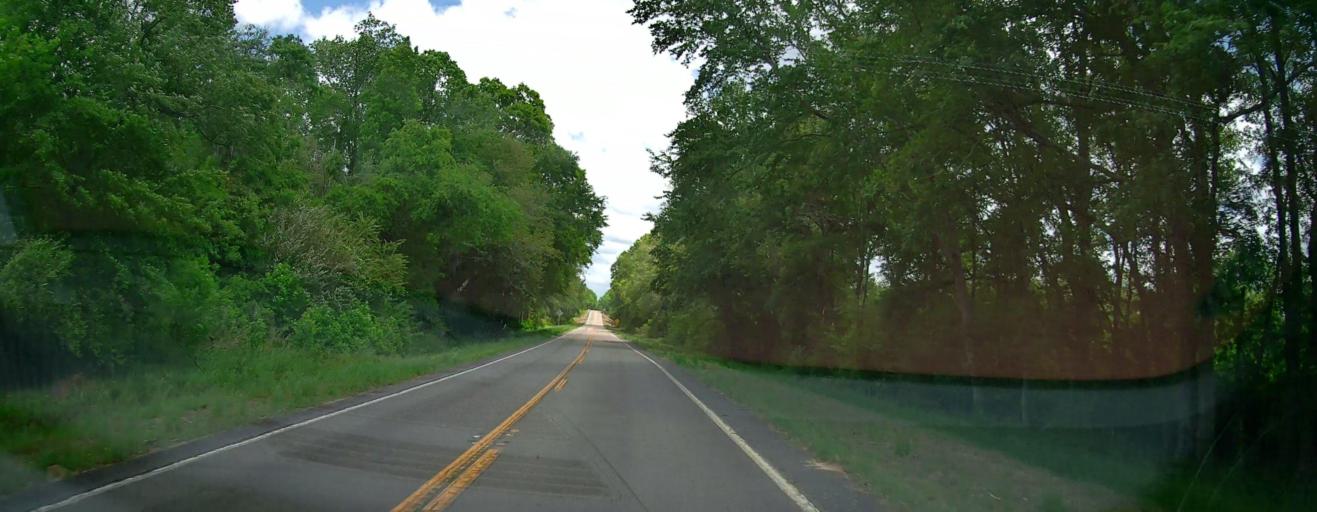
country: US
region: Georgia
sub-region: Dodge County
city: Chester
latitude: 32.5472
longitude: -83.1787
